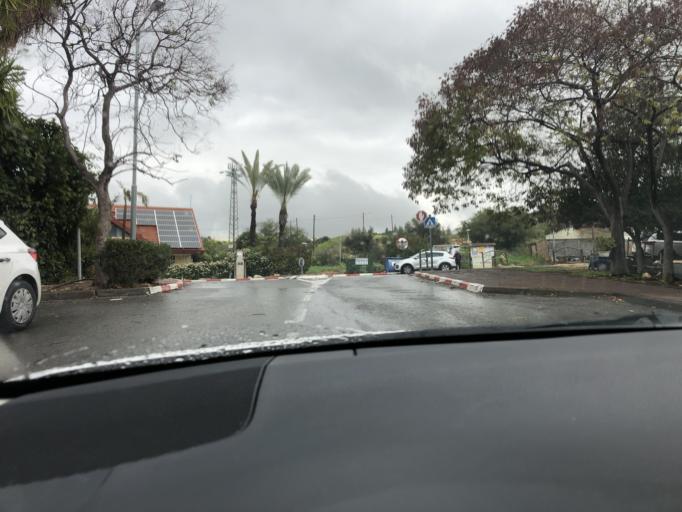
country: PS
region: West Bank
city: Azun Atme
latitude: 32.1132
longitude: 35.0312
